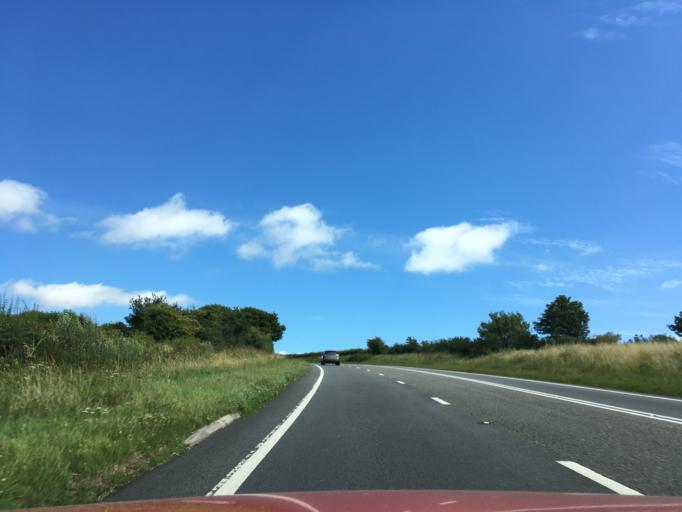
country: GB
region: England
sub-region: Somerset
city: Yeovil
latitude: 50.8293
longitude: -2.5706
